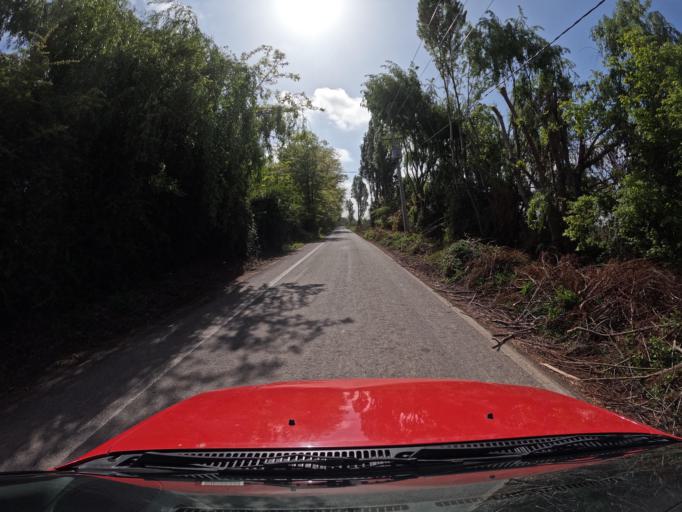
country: CL
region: Maule
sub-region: Provincia de Curico
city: Teno
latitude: -34.8816
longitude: -71.2425
